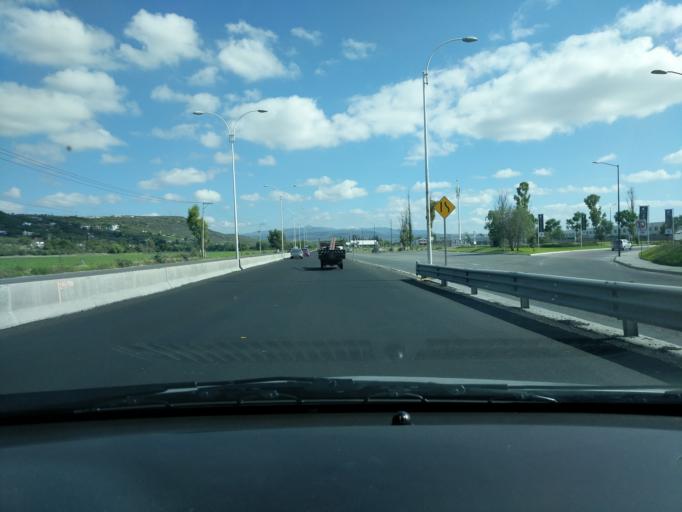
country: MX
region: Queretaro
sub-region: Queretaro
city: Patria Nueva
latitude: 20.6239
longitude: -100.4967
